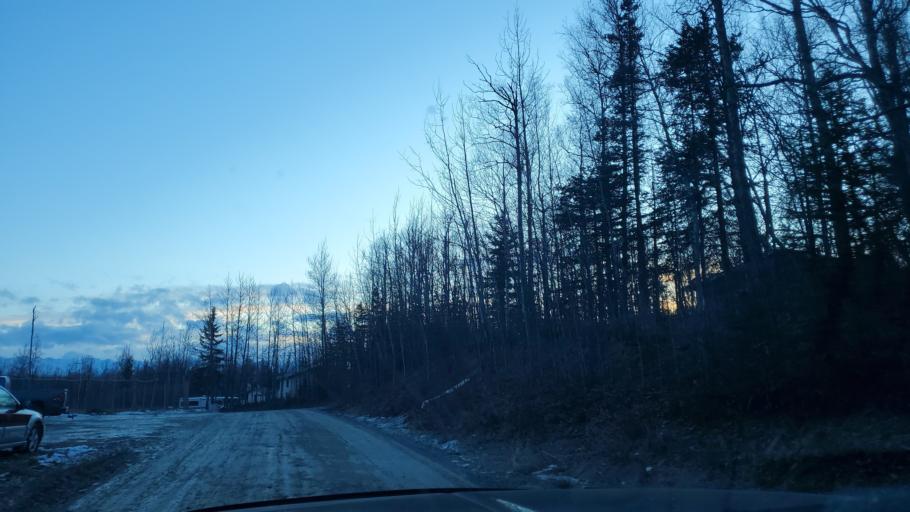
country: US
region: Alaska
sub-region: Matanuska-Susitna Borough
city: Tanaina
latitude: 61.6119
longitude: -149.4042
